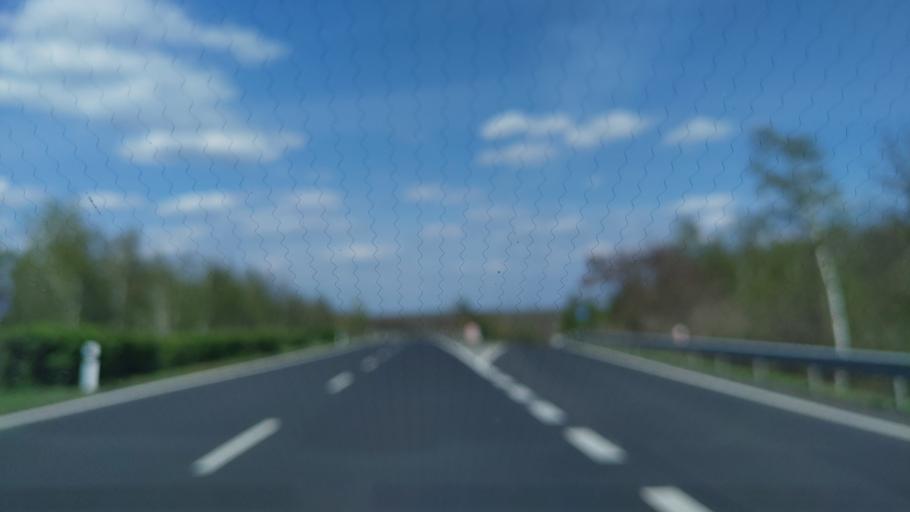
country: CZ
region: Ustecky
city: Horni Jiretin
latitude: 50.5216
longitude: 13.5414
